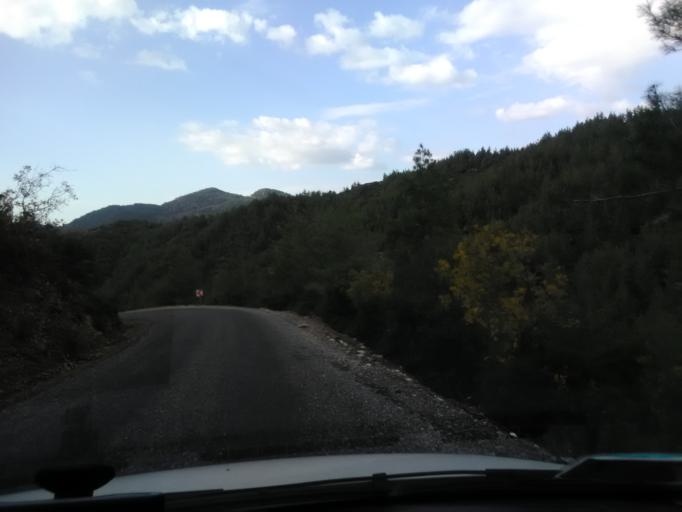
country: TR
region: Antalya
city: Gazipasa
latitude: 36.3050
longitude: 32.3969
